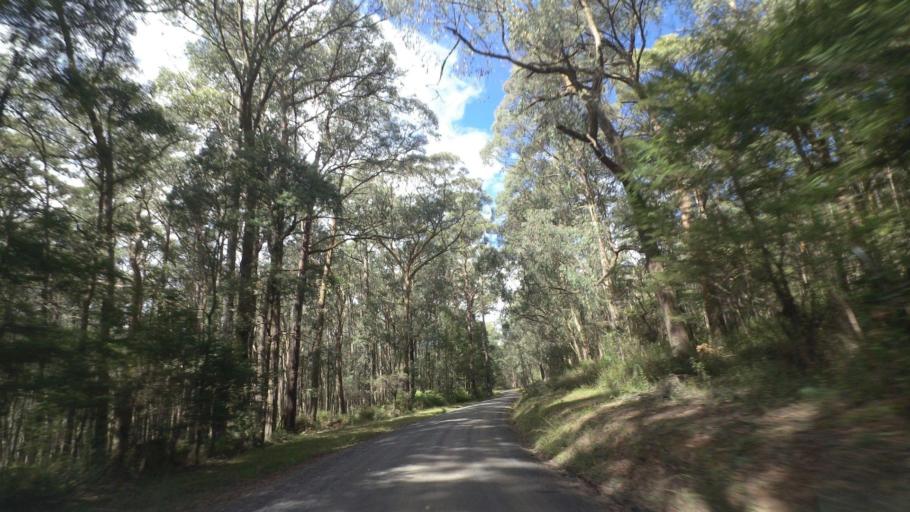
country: AU
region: Victoria
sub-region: Cardinia
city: Gembrook
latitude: -37.8844
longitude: 145.6186
